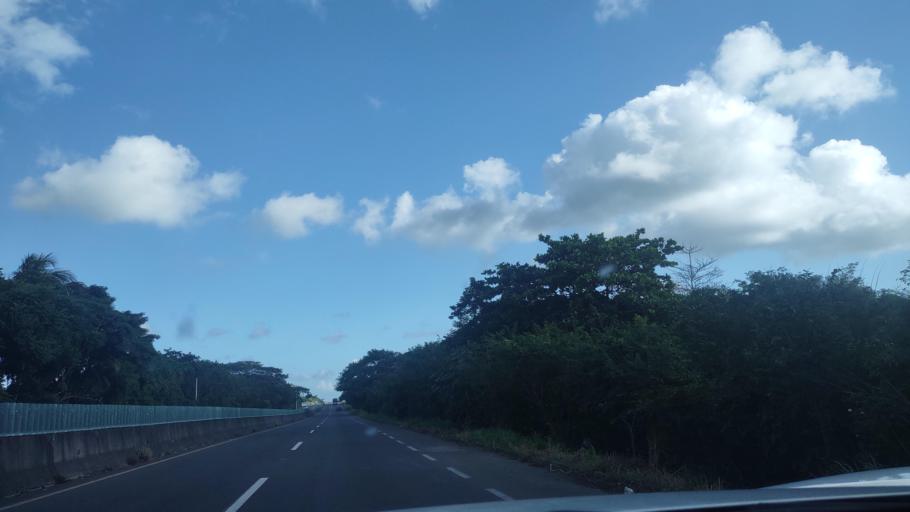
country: MX
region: Veracruz
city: El Tejar
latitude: 19.0625
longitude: -96.1744
